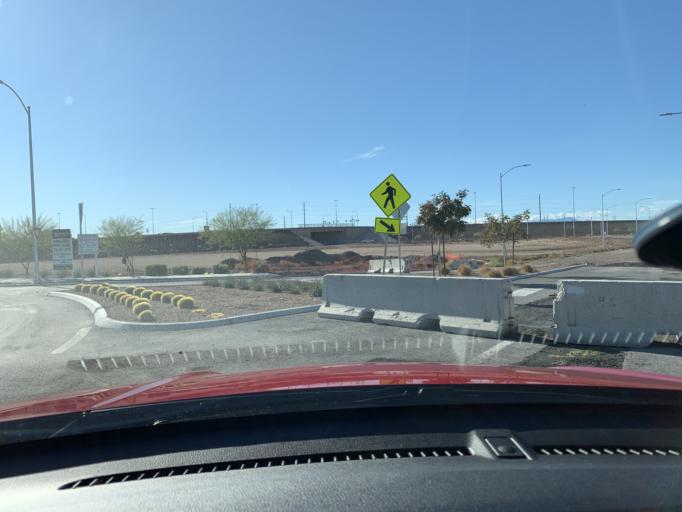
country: US
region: Nevada
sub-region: Clark County
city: Whitney
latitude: 36.0734
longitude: -115.0329
